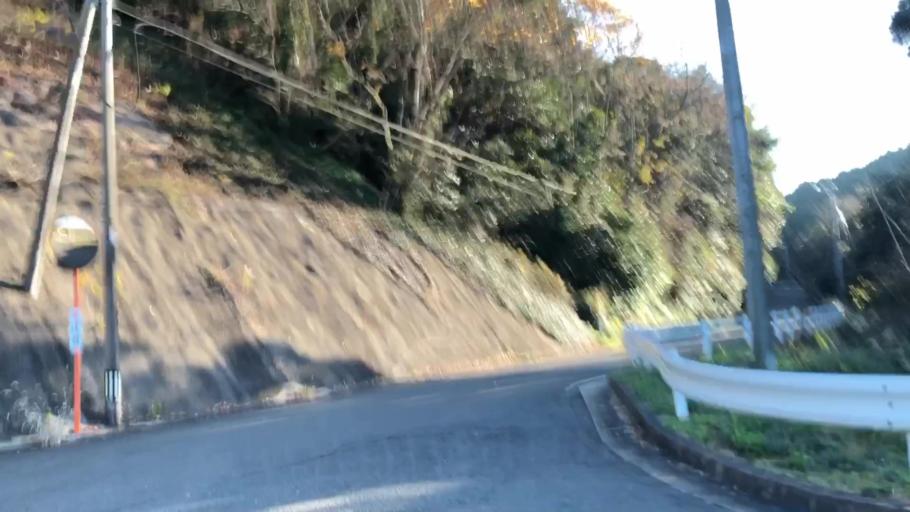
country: JP
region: Nagasaki
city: Sasebo
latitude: 33.0287
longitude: 129.6743
